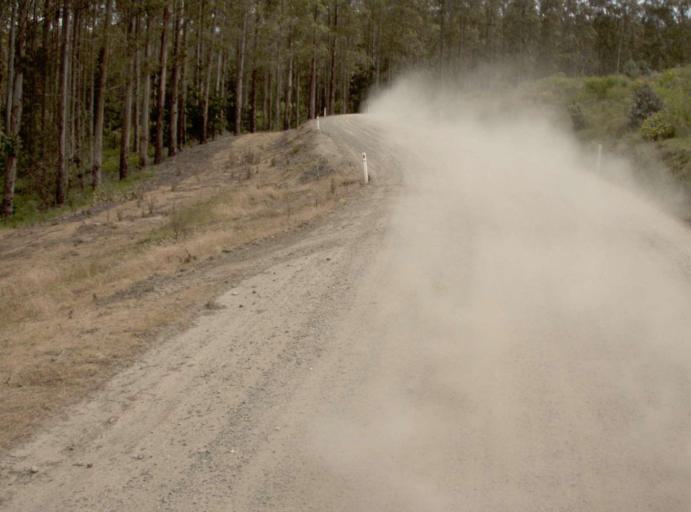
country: AU
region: Victoria
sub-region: Latrobe
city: Traralgon
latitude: -38.3743
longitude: 146.6801
